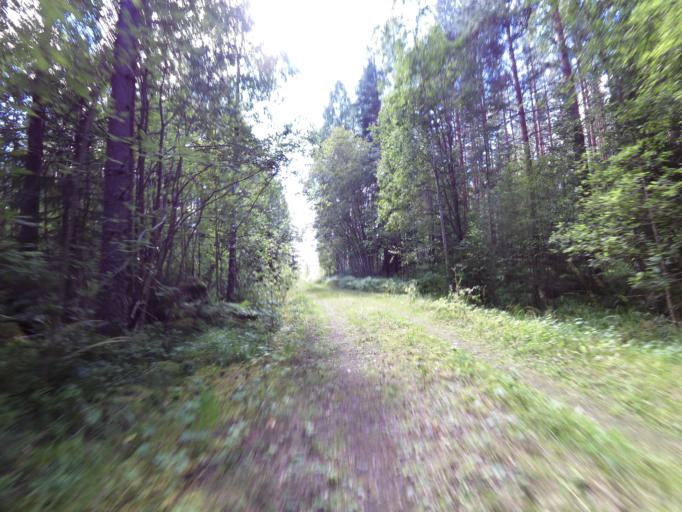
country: SE
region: Gaevleborg
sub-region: Hofors Kommun
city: Hofors
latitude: 60.5430
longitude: 16.2397
